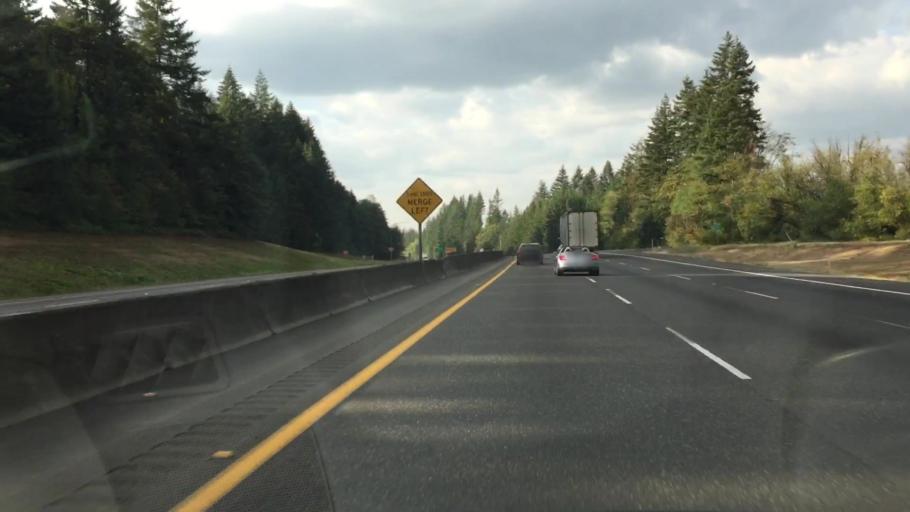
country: US
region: Washington
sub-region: Cowlitz County
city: Castle Rock
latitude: 46.3527
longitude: -122.9060
